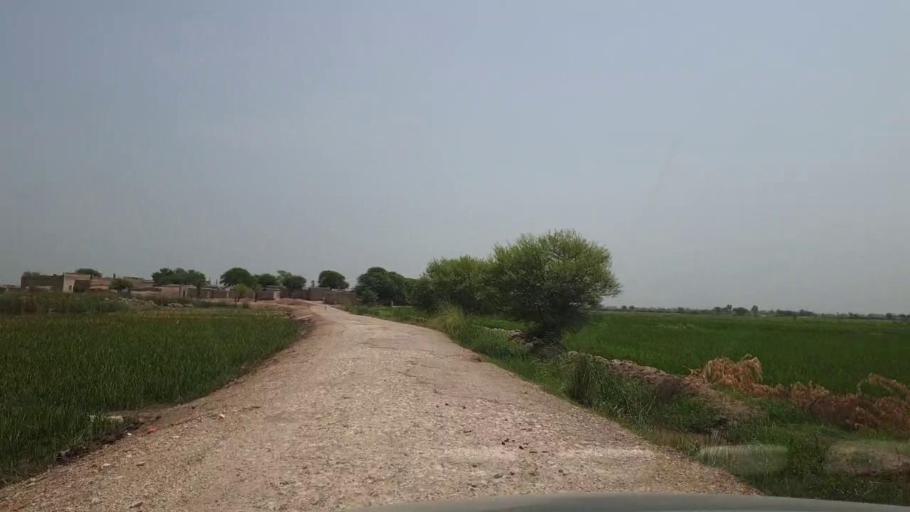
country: PK
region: Sindh
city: Garhi Yasin
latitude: 27.8697
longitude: 68.5032
